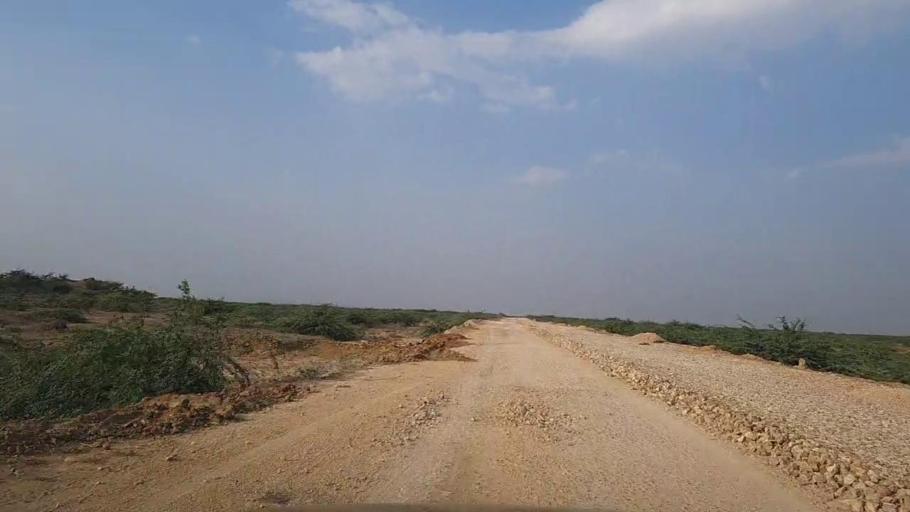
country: PK
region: Sindh
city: Gharo
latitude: 24.8337
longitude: 67.7455
